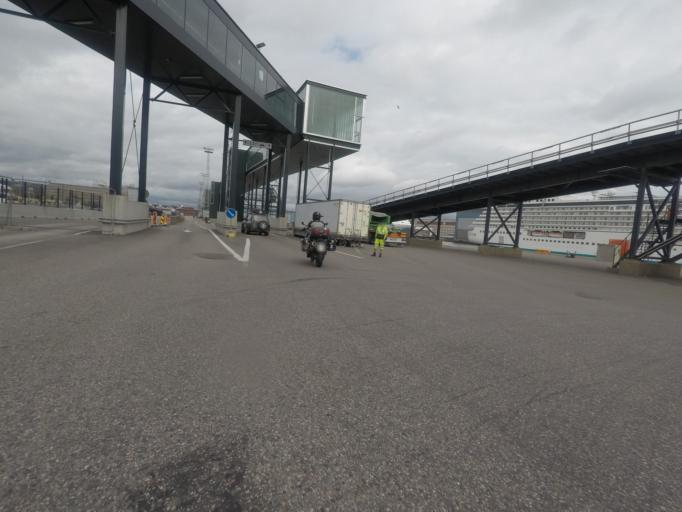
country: FI
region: Uusimaa
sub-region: Helsinki
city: Helsinki
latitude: 60.1498
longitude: 24.9162
